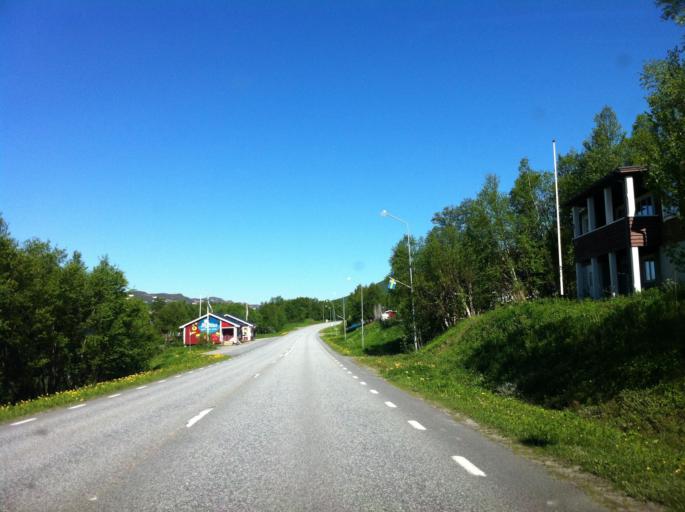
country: NO
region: Sor-Trondelag
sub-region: Tydal
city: Aas
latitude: 62.5401
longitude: 12.3422
